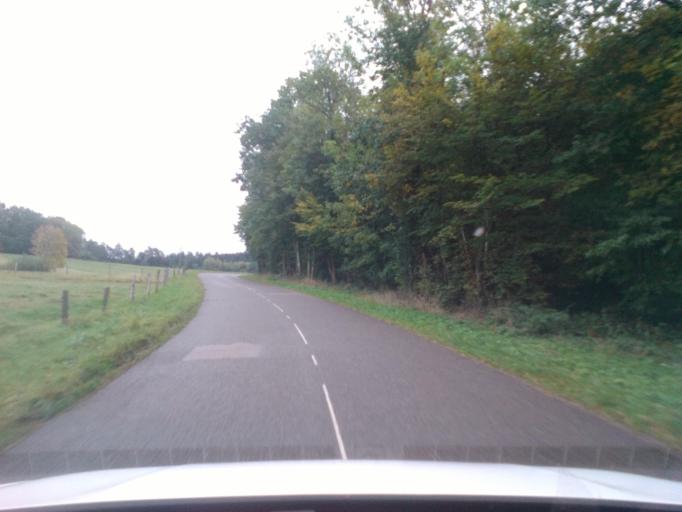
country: FR
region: Lorraine
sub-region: Departement des Vosges
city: Senones
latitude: 48.3673
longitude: 6.9620
